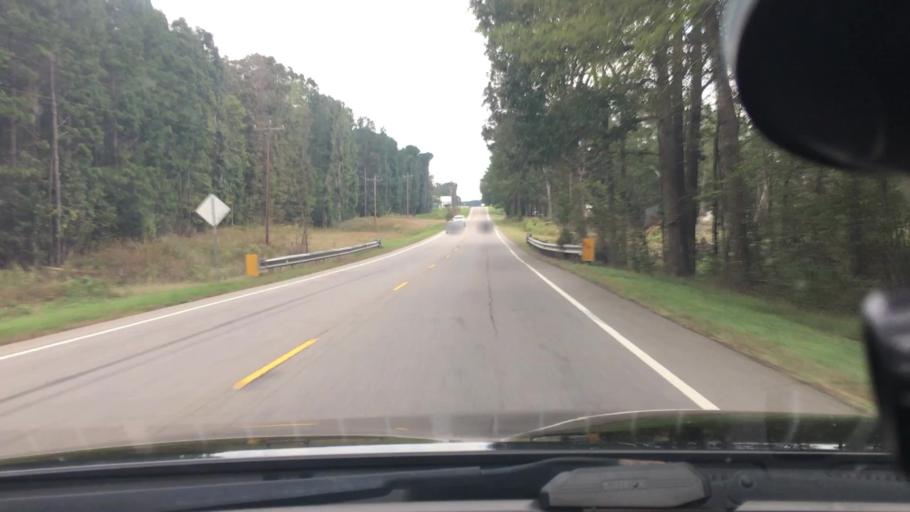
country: US
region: North Carolina
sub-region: Moore County
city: Carthage
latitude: 35.3875
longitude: -79.5020
